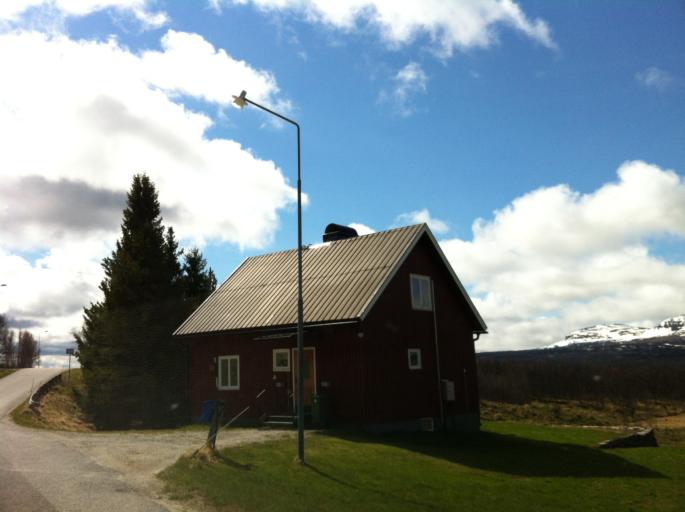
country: NO
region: Sor-Trondelag
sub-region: Tydal
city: Aas
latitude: 62.6452
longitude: 12.4398
